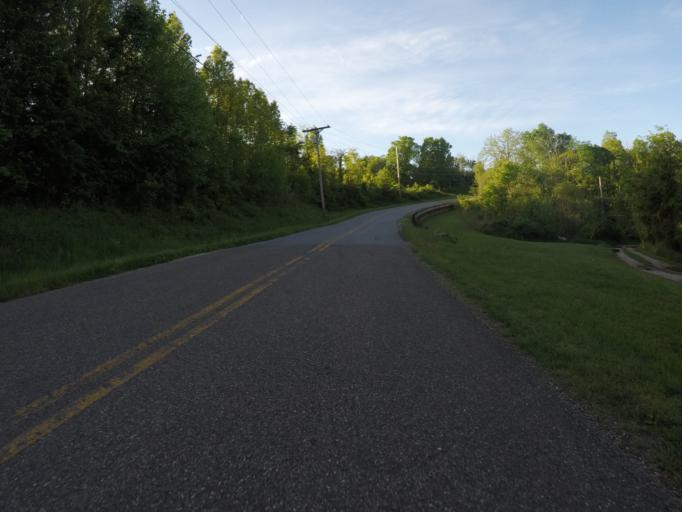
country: US
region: West Virginia
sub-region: Cabell County
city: Huntington
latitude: 38.5339
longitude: -82.4267
